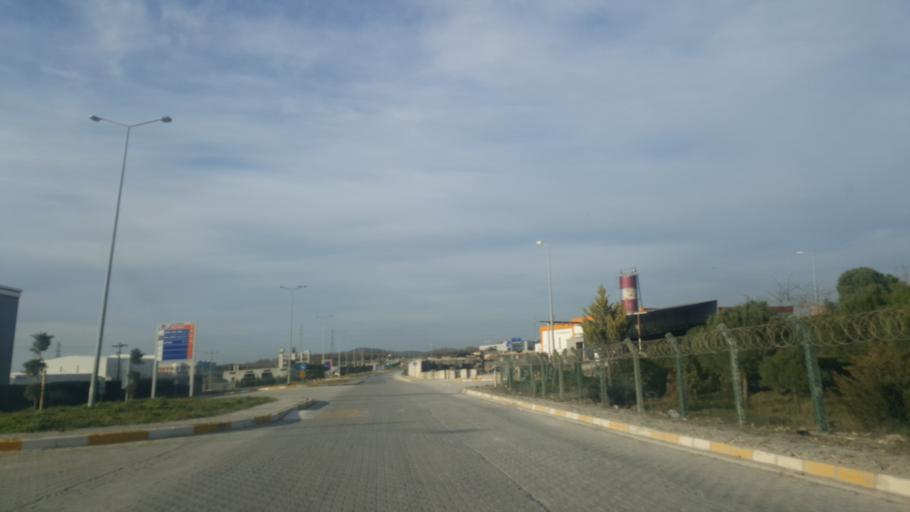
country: TR
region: Kocaeli
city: Mollafeneri
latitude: 40.8674
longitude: 29.5595
